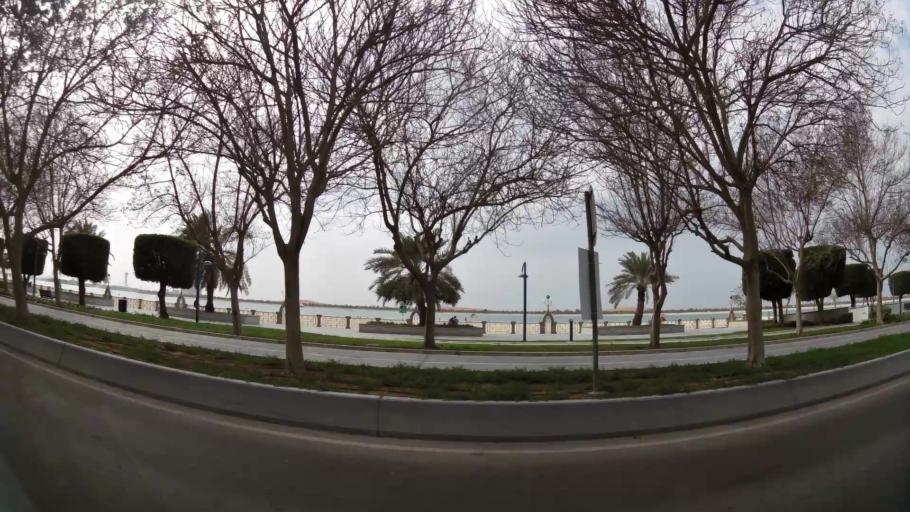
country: AE
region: Abu Dhabi
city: Abu Dhabi
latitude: 24.4859
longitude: 54.3492
